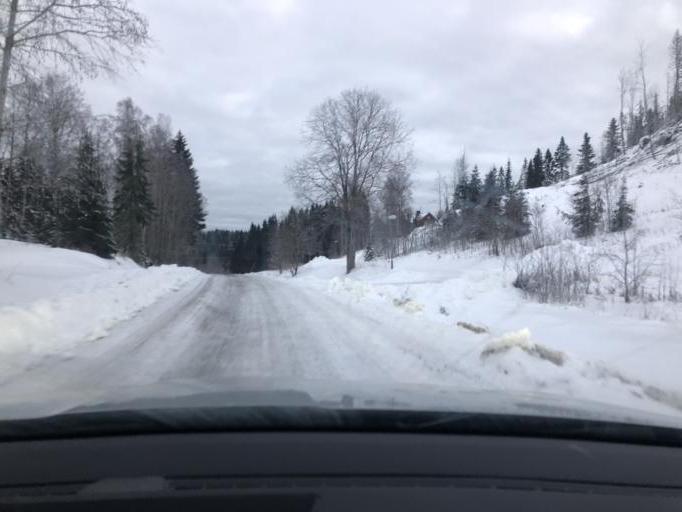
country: SE
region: Vaesternorrland
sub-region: Kramfors Kommun
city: Nordingra
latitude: 62.9065
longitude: 18.2411
